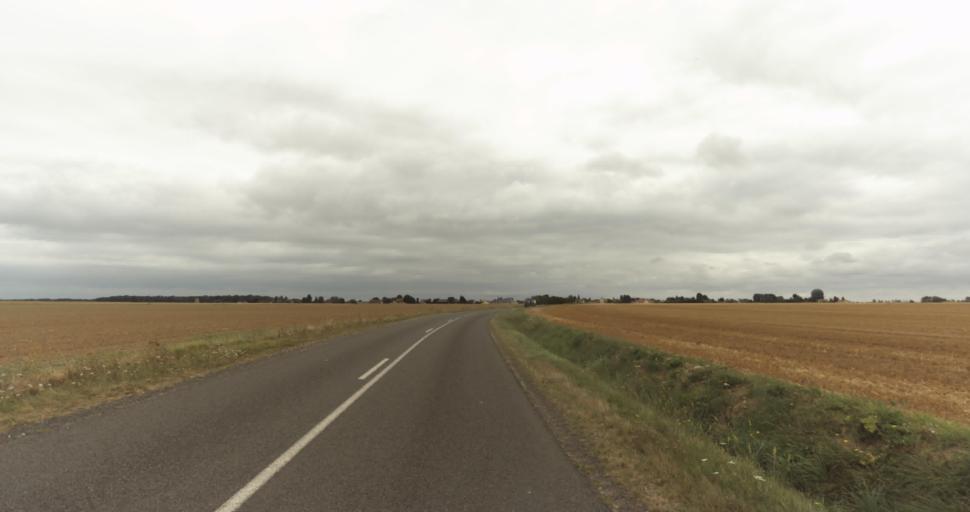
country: FR
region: Haute-Normandie
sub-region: Departement de l'Eure
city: Gravigny
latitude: 49.0395
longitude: 1.2380
